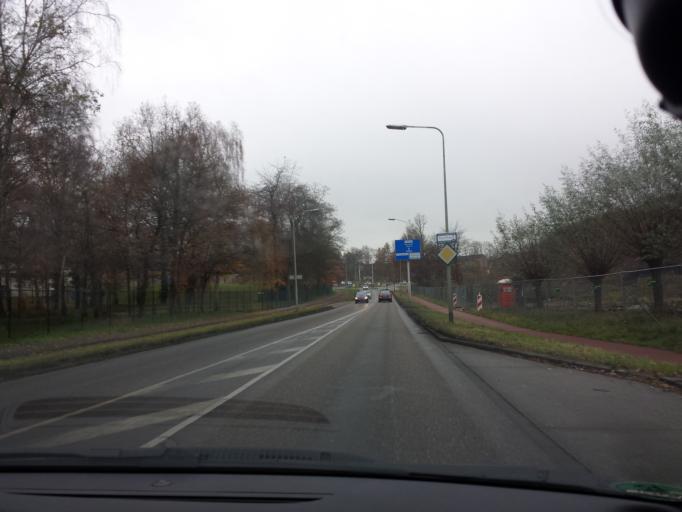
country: NL
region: Limburg
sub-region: Gemeente Brunssum
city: Brunssum
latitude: 50.9390
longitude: 5.9897
